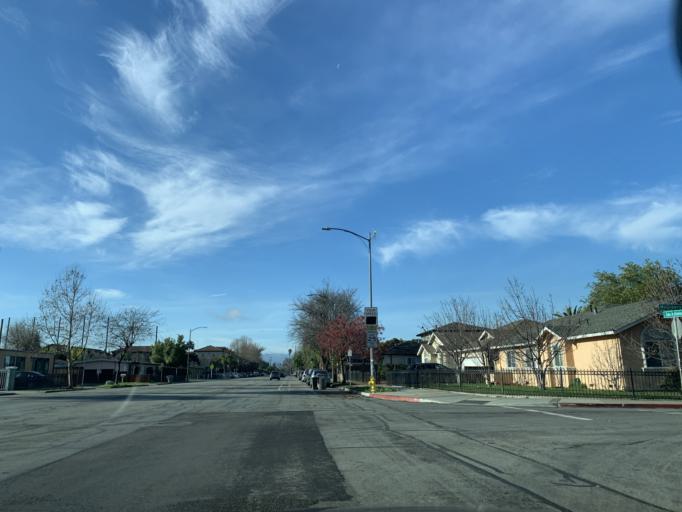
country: US
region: California
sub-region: Santa Clara County
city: Alum Rock
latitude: 37.3515
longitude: -121.8493
